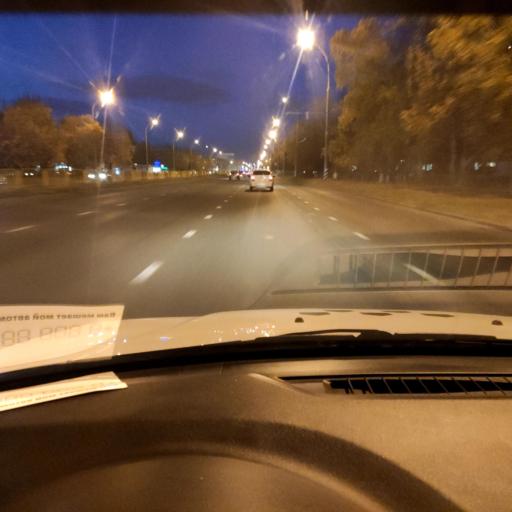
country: RU
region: Samara
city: Tol'yatti
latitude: 53.5311
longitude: 49.2980
